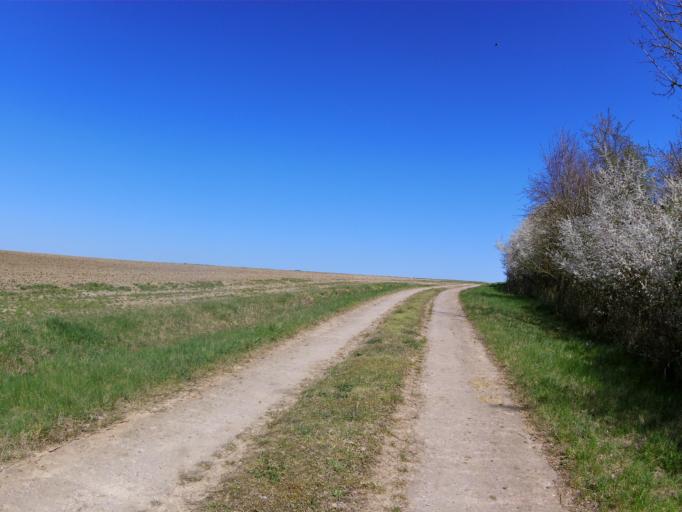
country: DE
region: Bavaria
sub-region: Regierungsbezirk Unterfranken
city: Rottendorf
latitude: 49.8179
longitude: 10.0695
